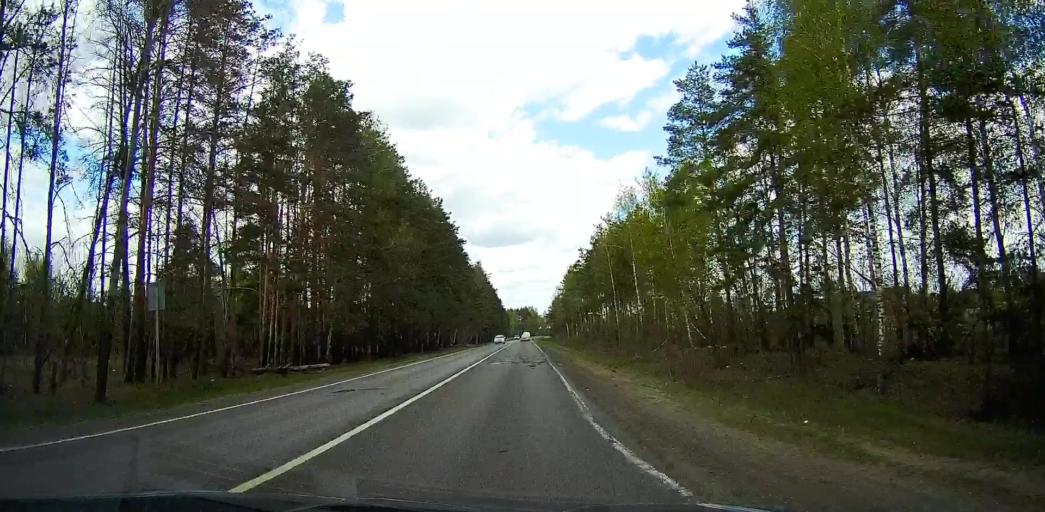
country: RU
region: Moskovskaya
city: Davydovo
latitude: 55.6267
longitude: 38.8612
